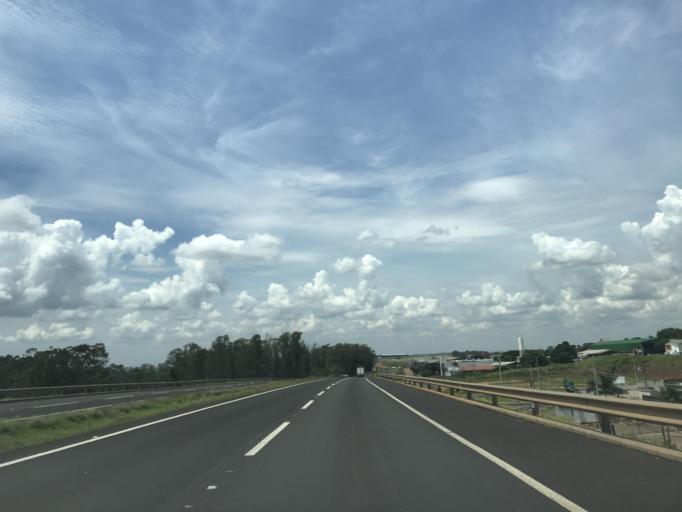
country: BR
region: Parana
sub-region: Alto Parana
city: Alto Parana
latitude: -23.2012
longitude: -52.1974
